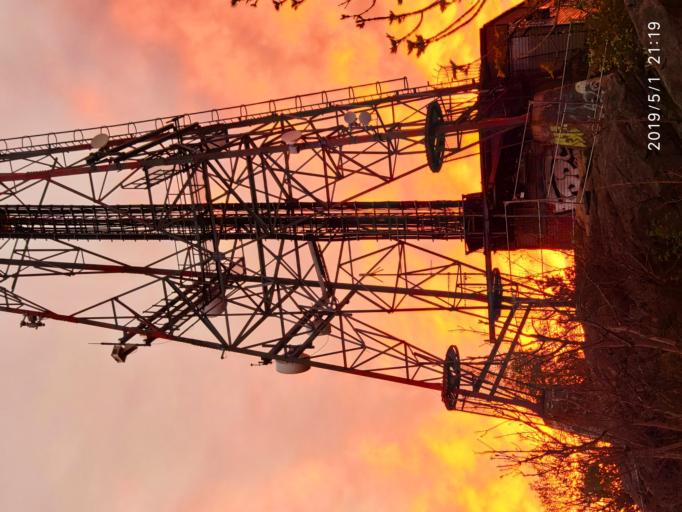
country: NO
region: Aust-Agder
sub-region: Arendal
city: Arendal
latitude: 58.4634
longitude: 8.7672
